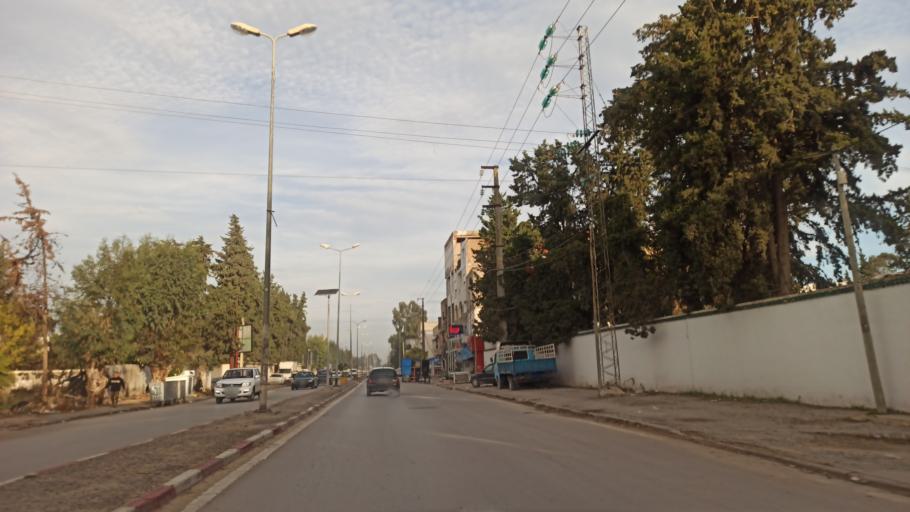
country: TN
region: Ariana
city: Ariana
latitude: 36.8689
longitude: 10.2498
